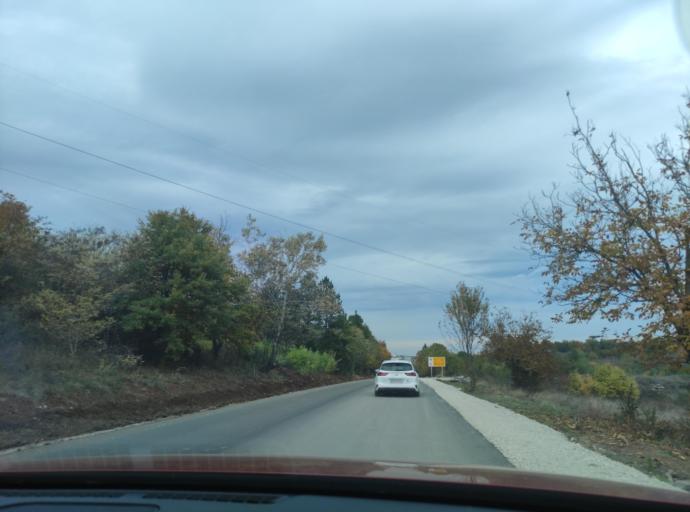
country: BG
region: Montana
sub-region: Obshtina Montana
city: Montana
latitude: 43.3909
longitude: 23.2418
